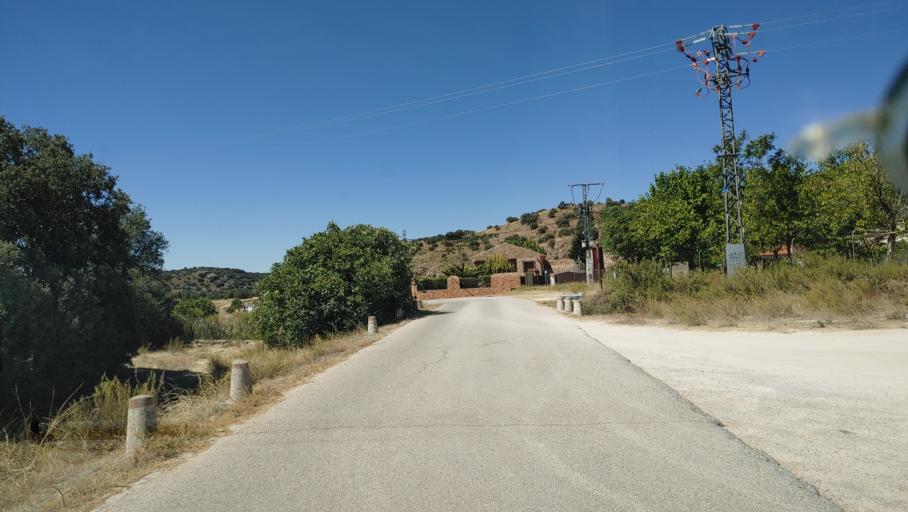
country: ES
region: Castille-La Mancha
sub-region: Provincia de Ciudad Real
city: Ruidera
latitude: 38.9263
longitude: -2.8291
